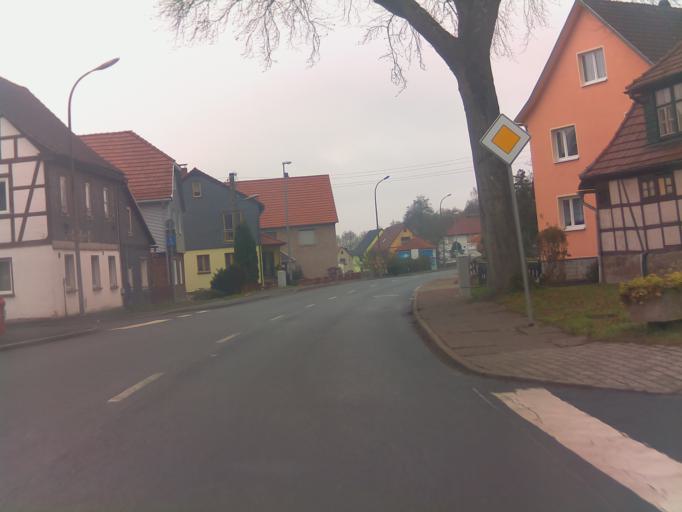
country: DE
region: Thuringia
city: Sankt Kilian
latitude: 50.5171
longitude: 10.7924
